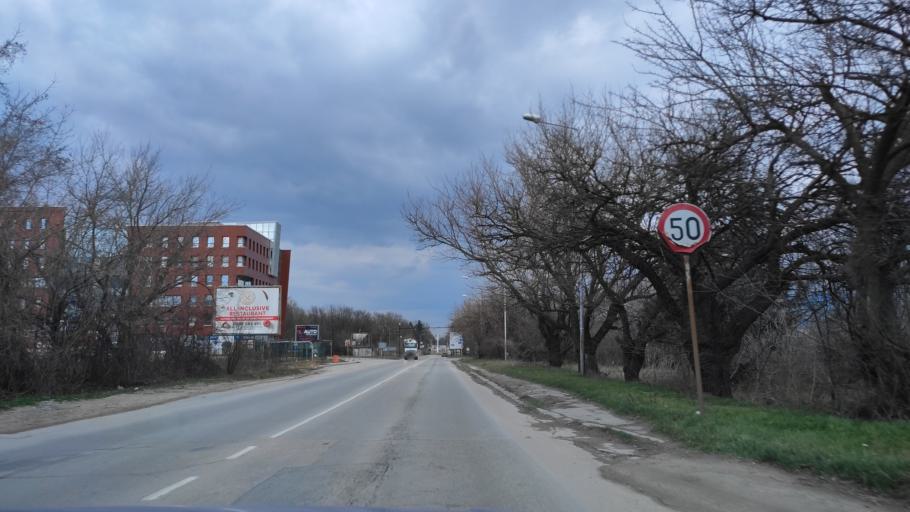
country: BG
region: Varna
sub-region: Obshtina Aksakovo
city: Aksakovo
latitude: 43.2267
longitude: 27.8554
